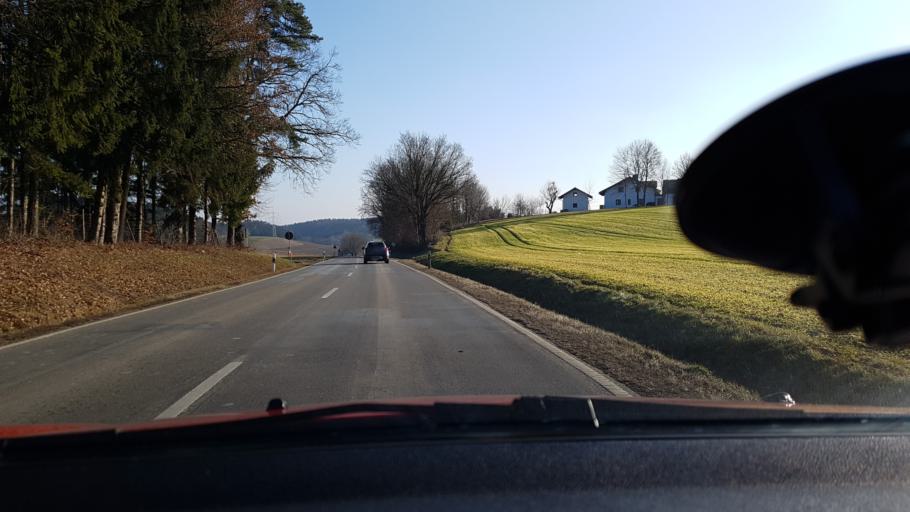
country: DE
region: Bavaria
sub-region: Lower Bavaria
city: Reut
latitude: 48.3131
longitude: 12.9530
